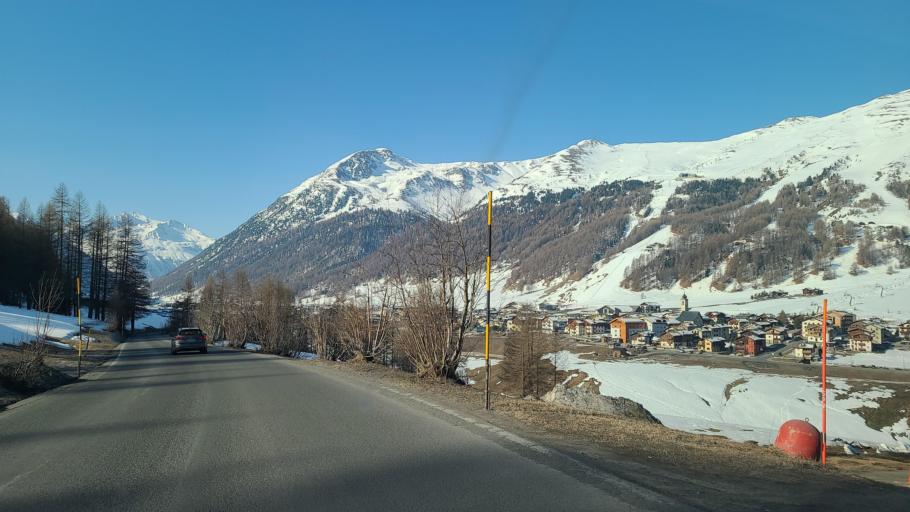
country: IT
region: Lombardy
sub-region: Provincia di Sondrio
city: Livigno
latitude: 46.5262
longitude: 10.1337
